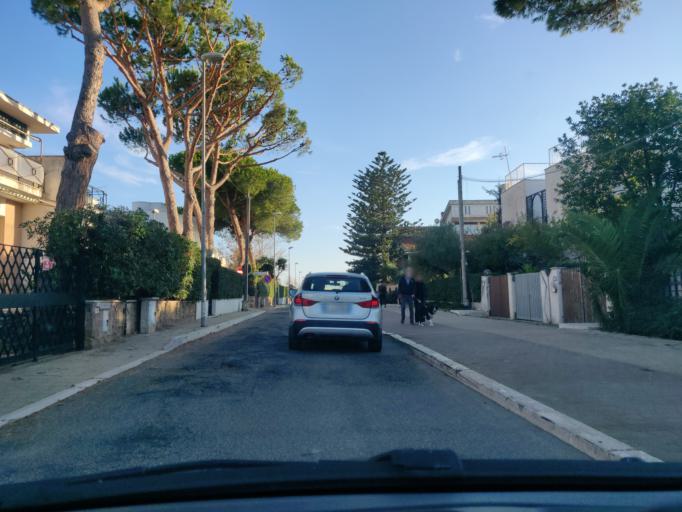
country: IT
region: Latium
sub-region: Citta metropolitana di Roma Capitale
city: Santa Marinella
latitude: 42.0321
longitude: 11.8343
